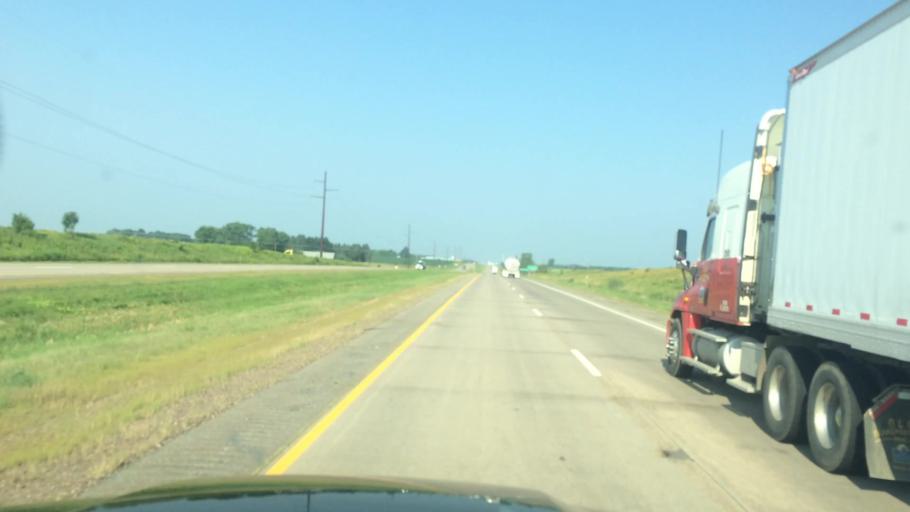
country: US
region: Wisconsin
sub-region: Marathon County
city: Edgar
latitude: 44.9444
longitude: -89.9874
